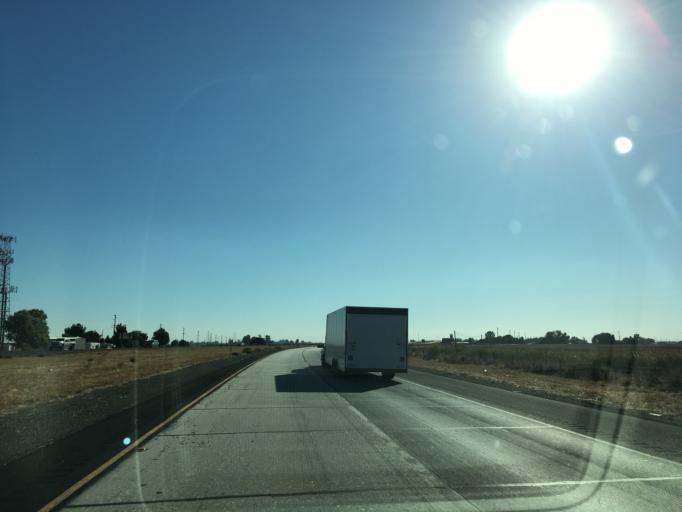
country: US
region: California
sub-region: Merced County
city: Dos Palos
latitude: 37.0540
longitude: -120.6499
